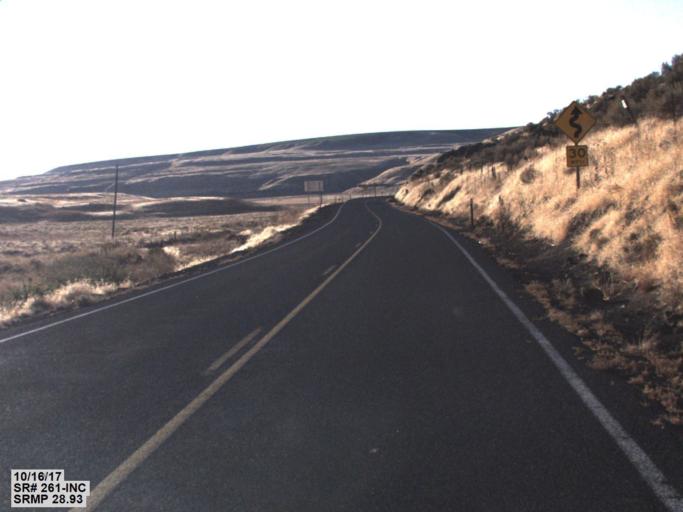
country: US
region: Washington
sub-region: Adams County
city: Ritzville
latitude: 46.6987
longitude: -118.4040
